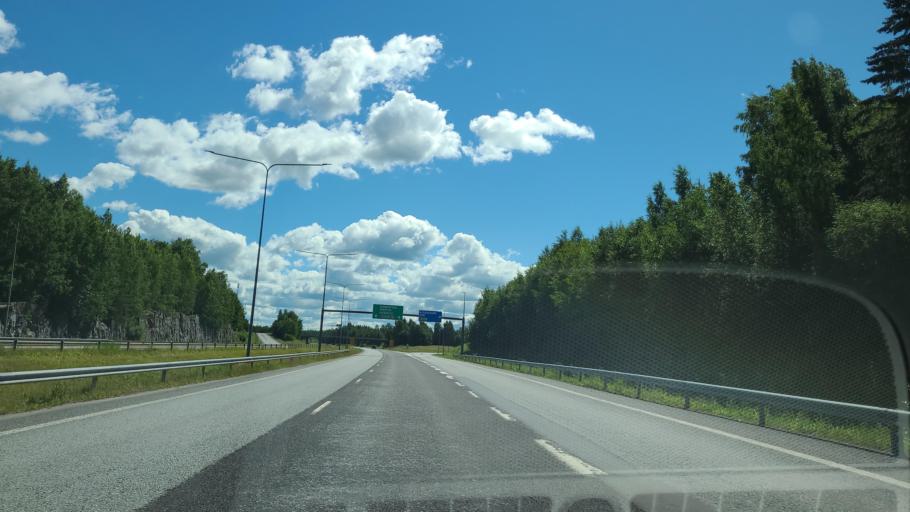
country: FI
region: Ostrobothnia
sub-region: Vaasa
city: Ristinummi
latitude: 63.0314
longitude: 21.7481
